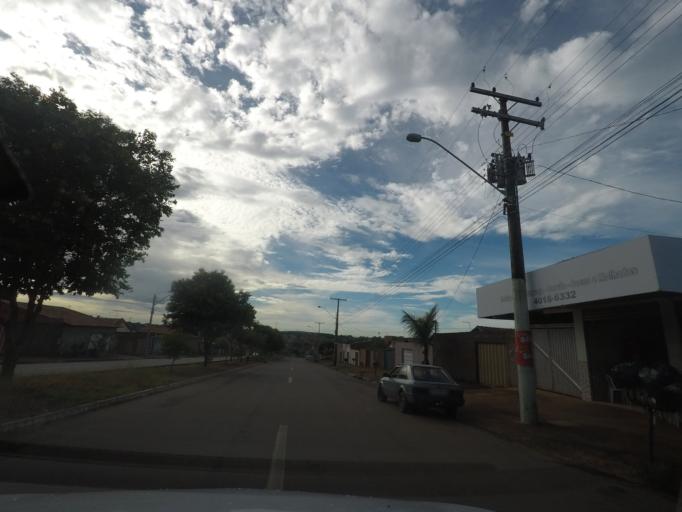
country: BR
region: Goias
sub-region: Aparecida De Goiania
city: Aparecida de Goiania
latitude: -16.7833
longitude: -49.3824
